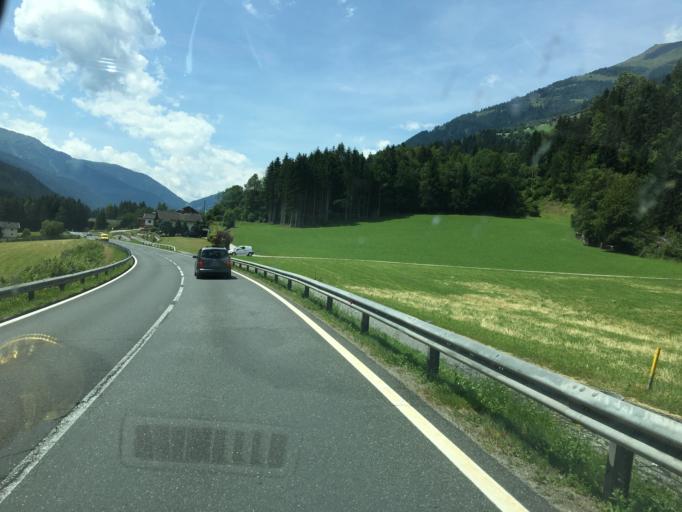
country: AT
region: Carinthia
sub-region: Politischer Bezirk Spittal an der Drau
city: Stall
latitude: 46.8823
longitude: 13.0167
